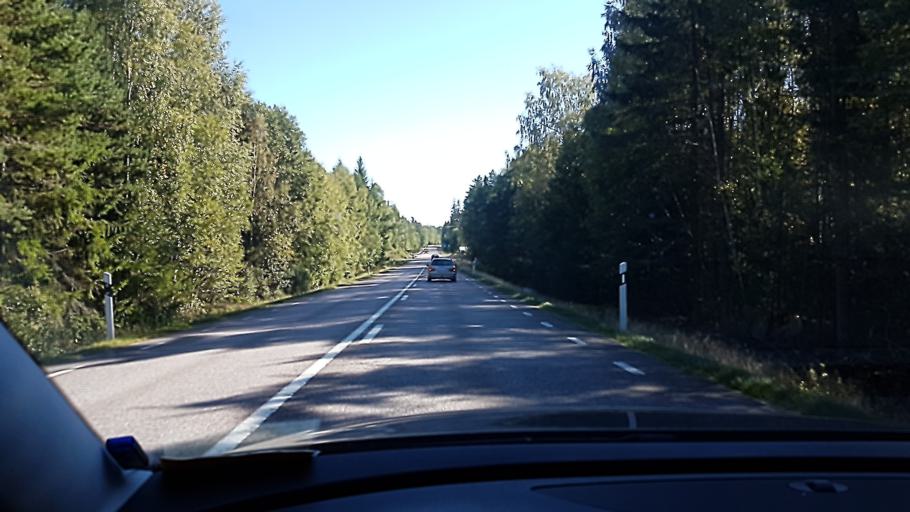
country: SE
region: Kronoberg
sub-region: Lessebo Kommun
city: Hovmantorp
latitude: 56.7857
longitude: 15.1677
